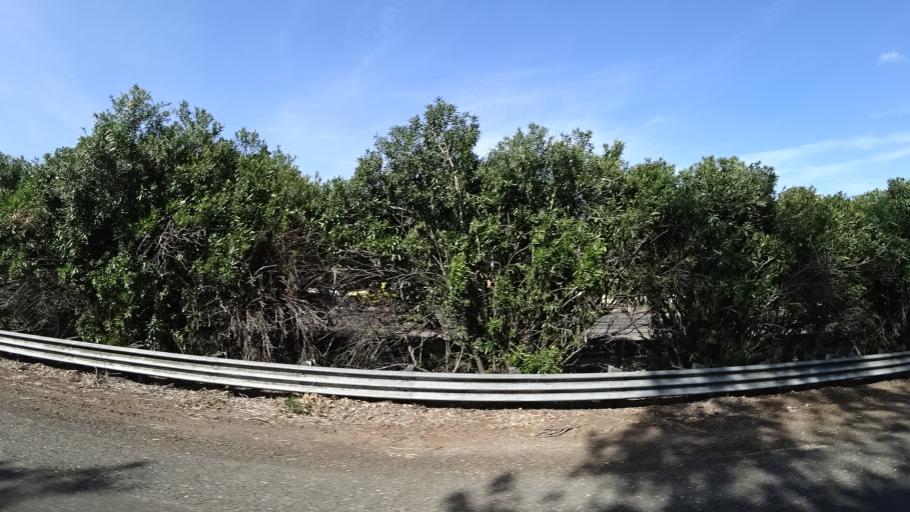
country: US
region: California
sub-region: Butte County
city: Chico
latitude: 39.7523
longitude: -121.8419
